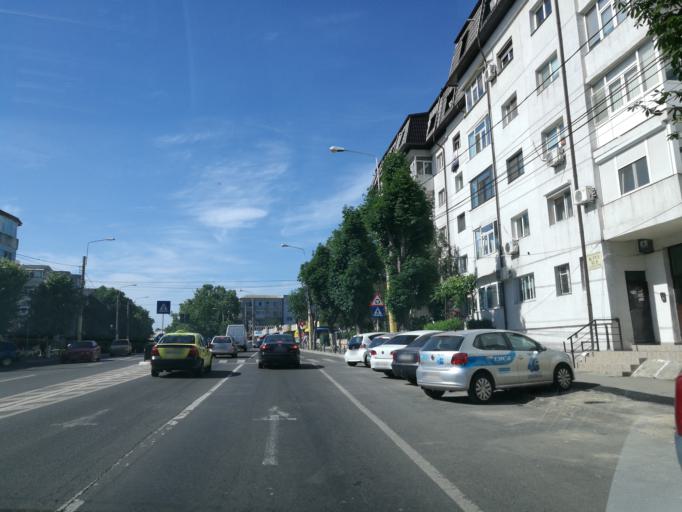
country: RO
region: Constanta
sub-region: Municipiul Constanta
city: Constanta
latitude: 44.1973
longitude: 28.6240
